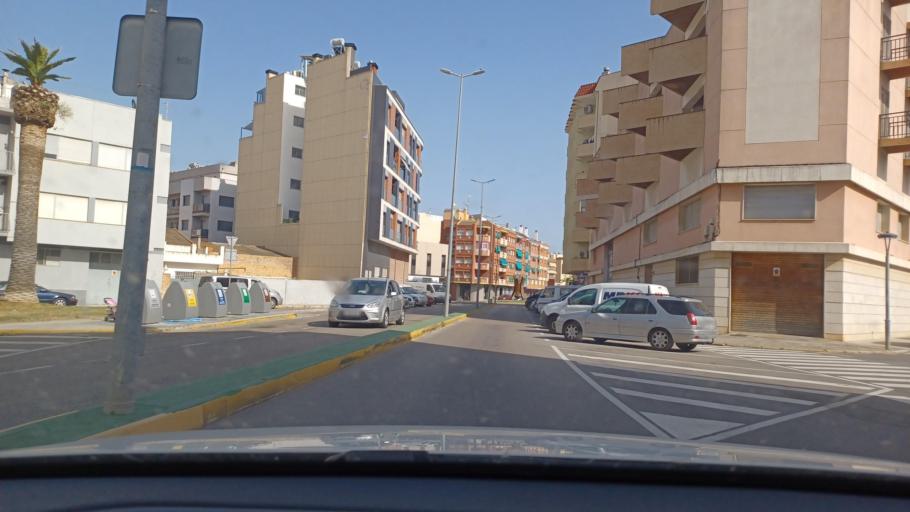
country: ES
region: Catalonia
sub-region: Provincia de Tarragona
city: Amposta
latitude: 40.7071
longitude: 0.5771
